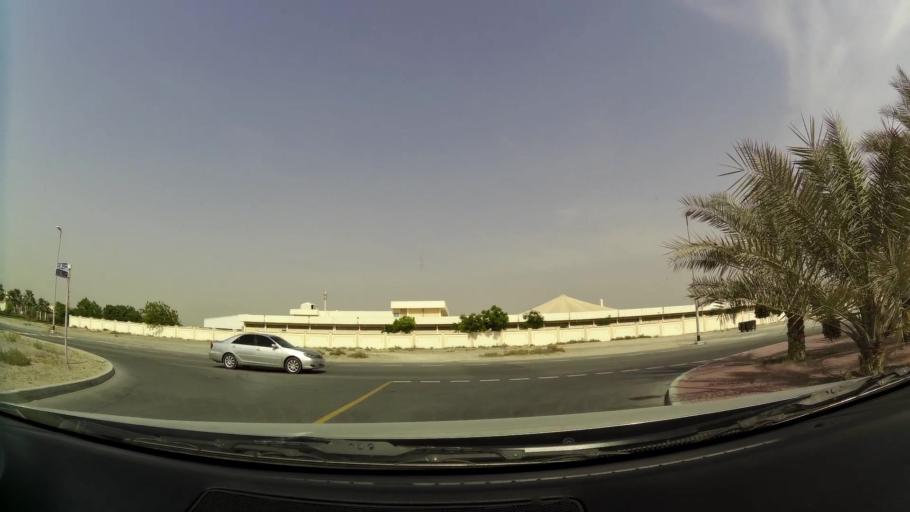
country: AE
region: Ash Shariqah
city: Sharjah
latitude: 25.2512
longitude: 55.4343
